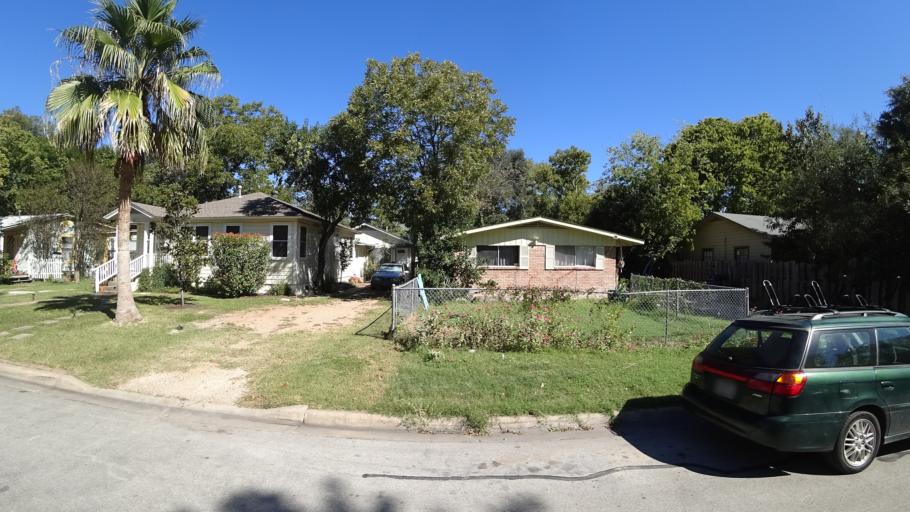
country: US
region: Texas
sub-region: Travis County
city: Austin
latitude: 30.3205
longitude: -97.7257
